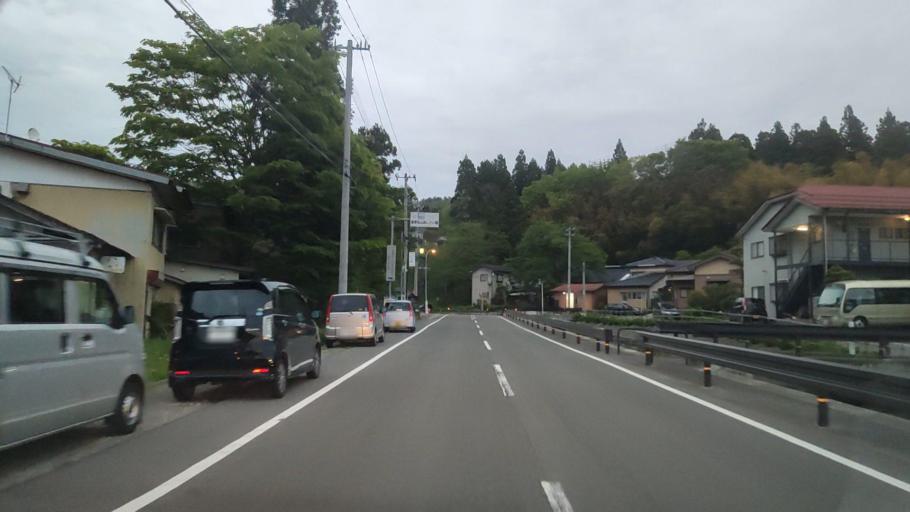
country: JP
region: Niigata
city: Kamo
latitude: 37.7119
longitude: 139.0767
